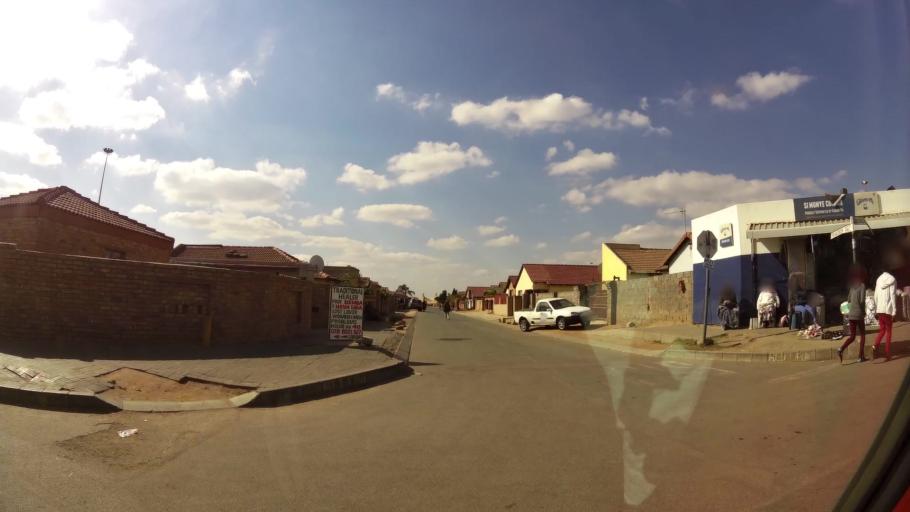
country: ZA
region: Gauteng
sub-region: Ekurhuleni Metropolitan Municipality
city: Tembisa
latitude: -26.0020
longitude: 28.2093
